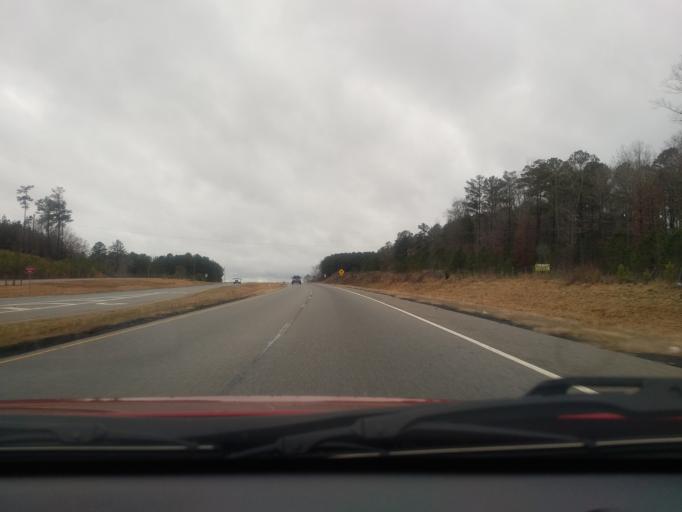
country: US
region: Georgia
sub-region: Henry County
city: Locust Grove
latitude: 33.2585
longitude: -84.1345
